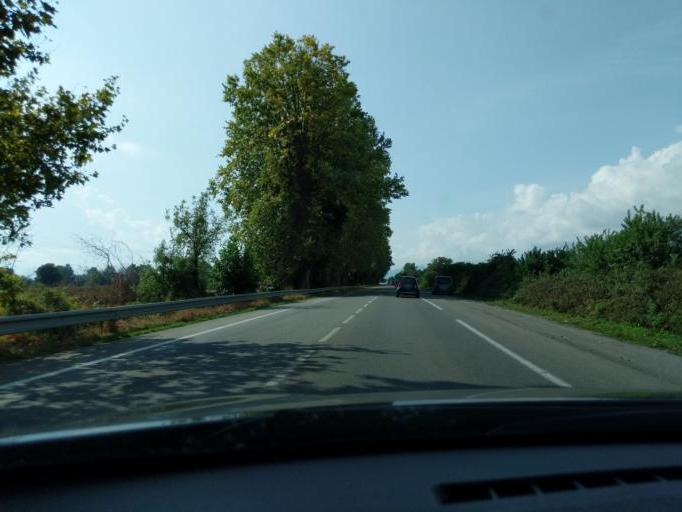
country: FR
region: Corsica
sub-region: Departement de la Haute-Corse
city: Ghisonaccia
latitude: 41.9806
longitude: 9.4001
